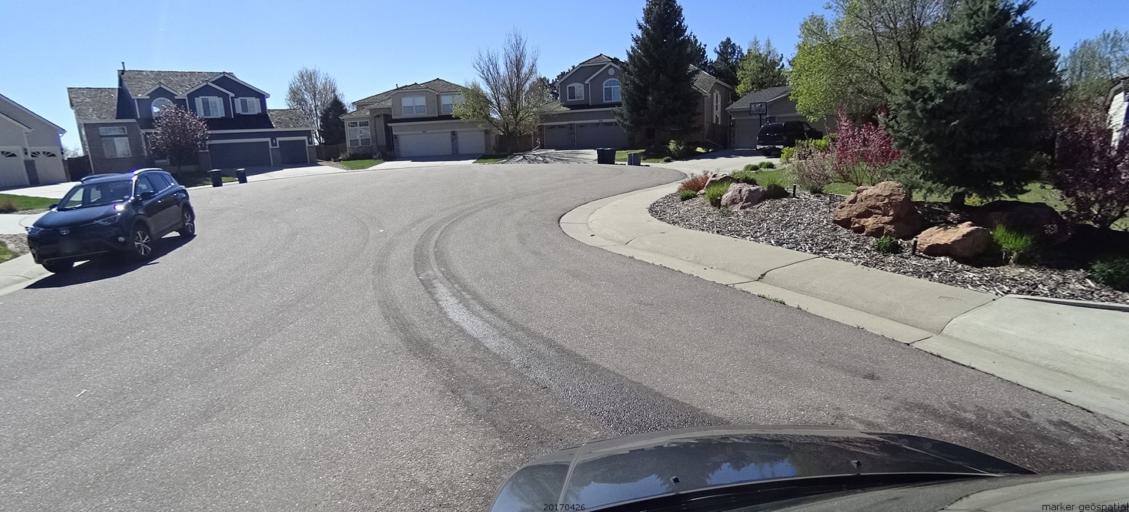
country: US
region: Colorado
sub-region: Douglas County
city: Carriage Club
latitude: 39.5374
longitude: -104.9032
